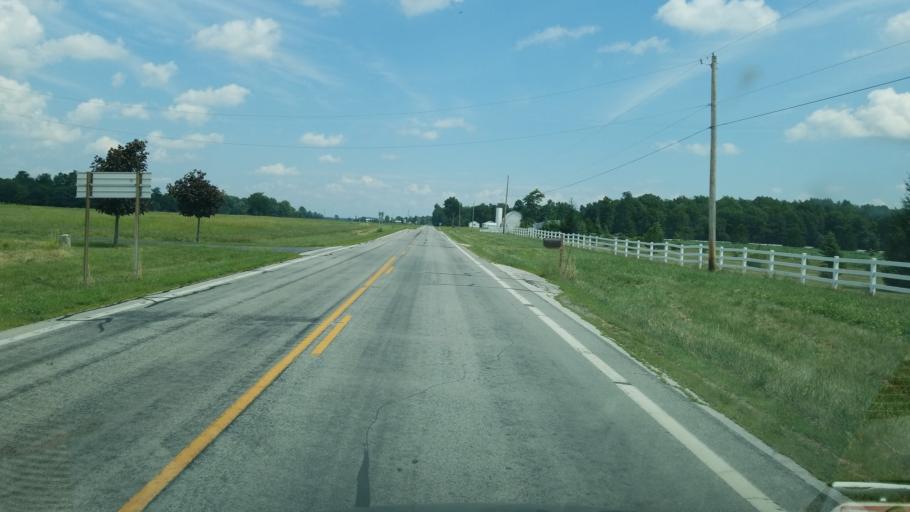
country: US
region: Ohio
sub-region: Hancock County
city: Arlington
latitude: 40.9204
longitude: -83.5544
